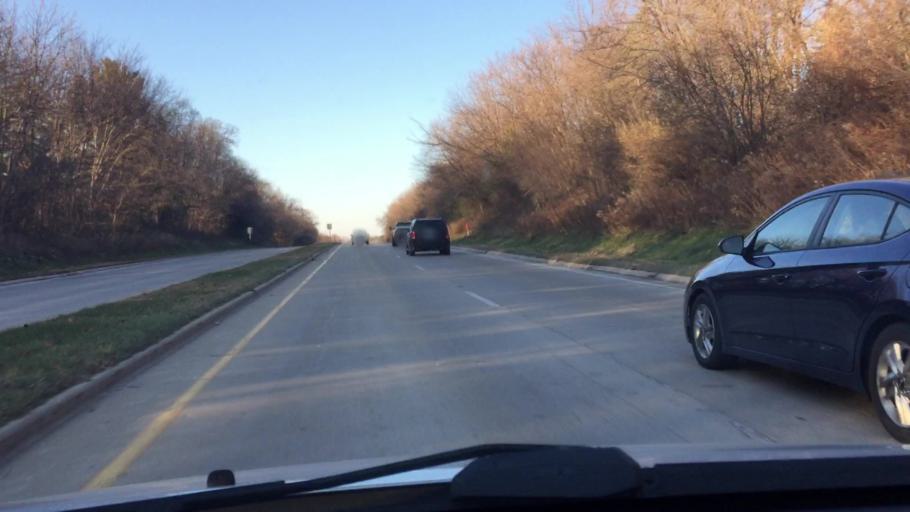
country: US
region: Wisconsin
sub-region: Waukesha County
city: Oconomowoc
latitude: 43.0999
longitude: -88.4803
